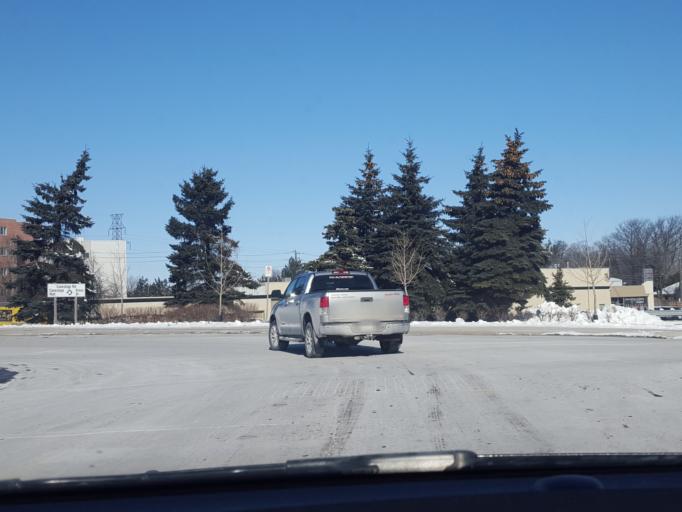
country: CA
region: Ontario
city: Waterloo
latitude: 43.4998
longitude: -80.5279
